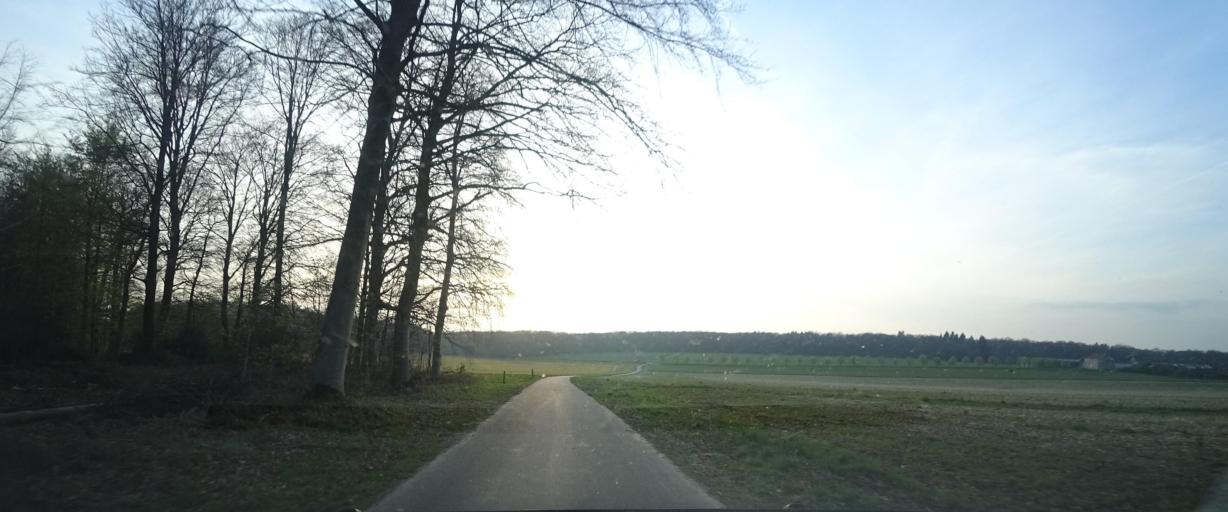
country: BE
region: Wallonia
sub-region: Province de Namur
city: Havelange
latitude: 50.3350
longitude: 5.2231
